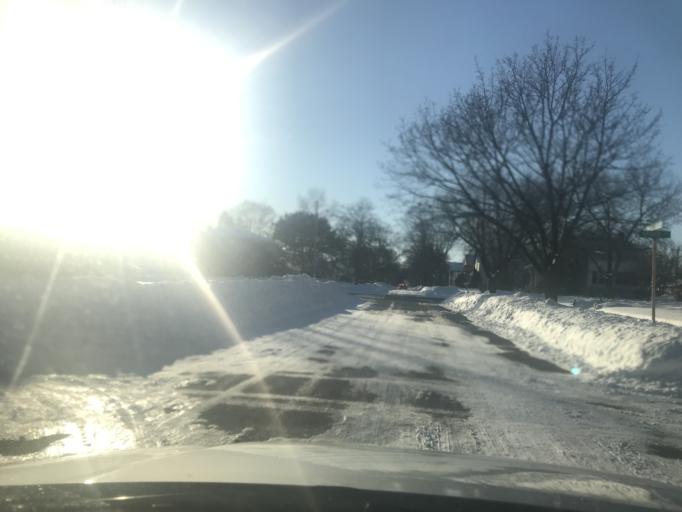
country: US
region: Wisconsin
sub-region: Marinette County
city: Marinette
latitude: 45.1004
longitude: -87.6439
